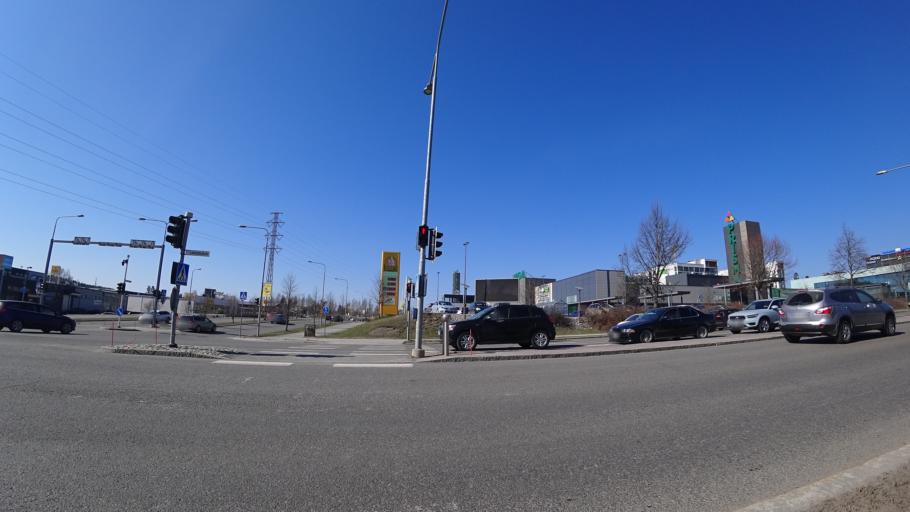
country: FI
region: Pirkanmaa
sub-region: Tampere
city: Pirkkala
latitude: 61.5183
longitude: 23.6676
